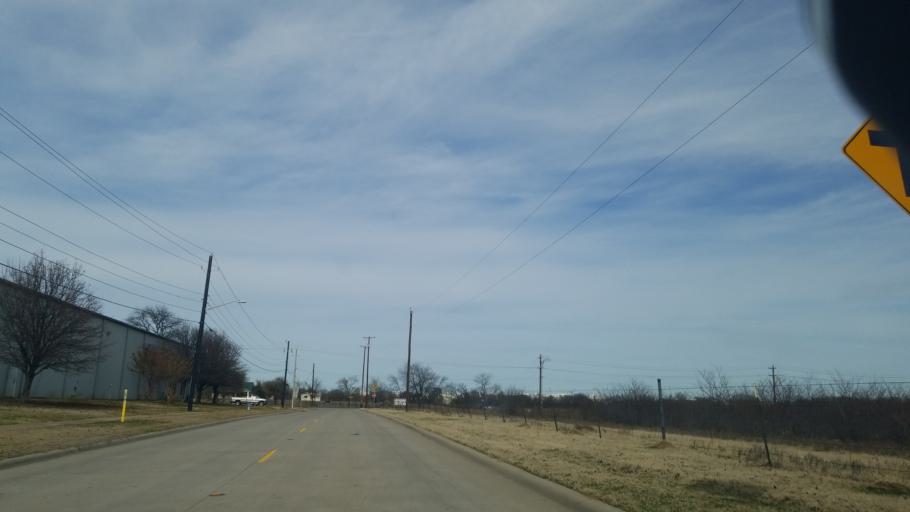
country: US
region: Texas
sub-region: Denton County
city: Denton
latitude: 33.2004
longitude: -97.1906
